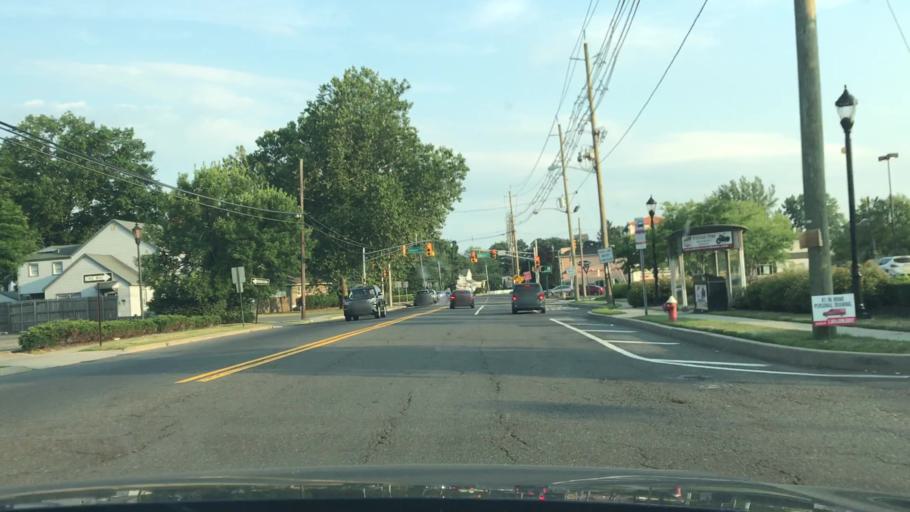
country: US
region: New Jersey
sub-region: Bergen County
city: Emerson
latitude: 40.9824
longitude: -74.0244
